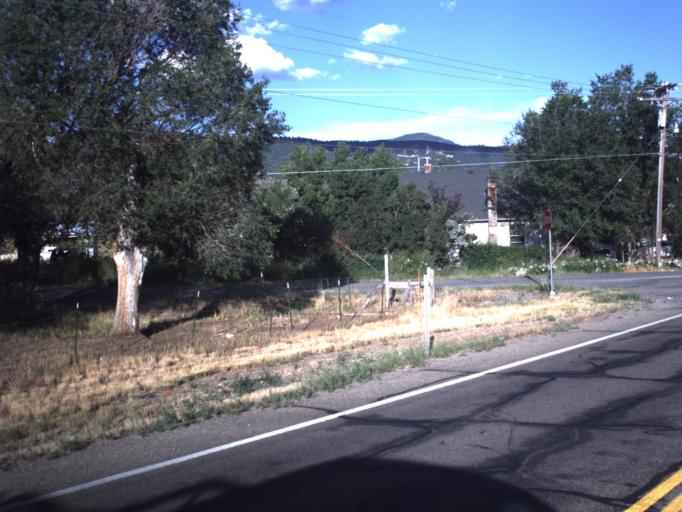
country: US
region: Utah
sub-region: Sanpete County
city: Fairview
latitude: 39.6361
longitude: -111.4437
